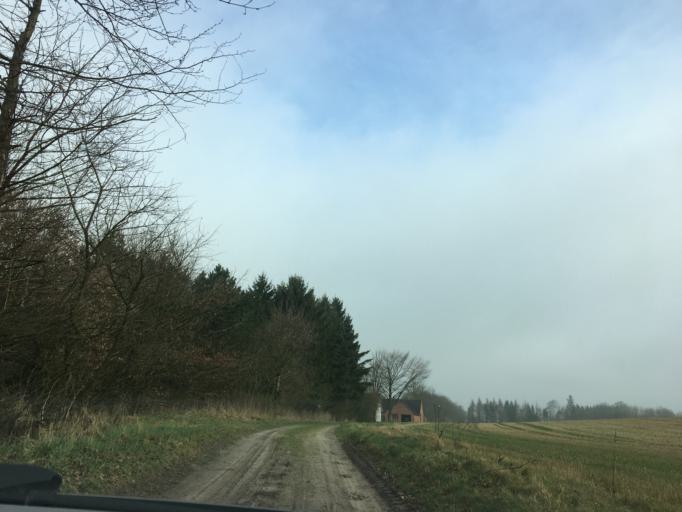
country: DK
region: South Denmark
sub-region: Vejle Kommune
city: Give
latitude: 55.8102
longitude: 9.3046
